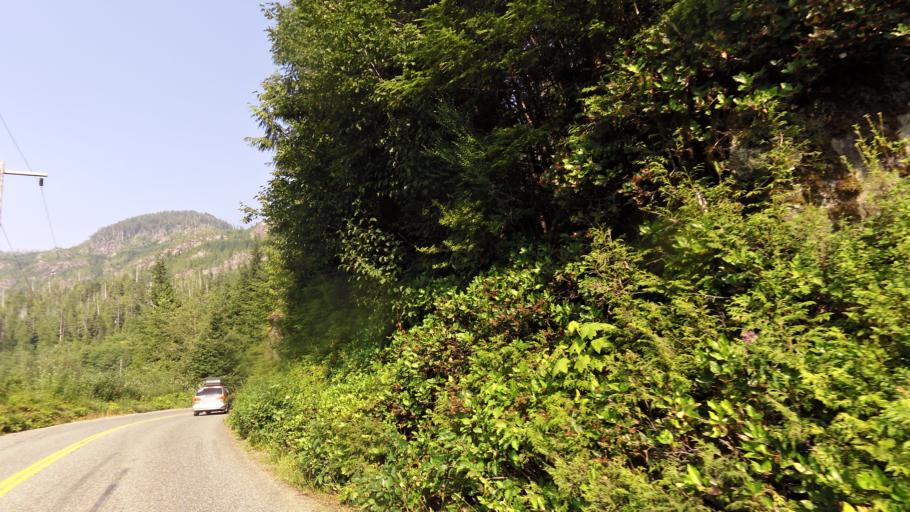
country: CA
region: British Columbia
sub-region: Regional District of Alberni-Clayoquot
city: Ucluelet
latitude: 49.0821
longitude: -125.4595
